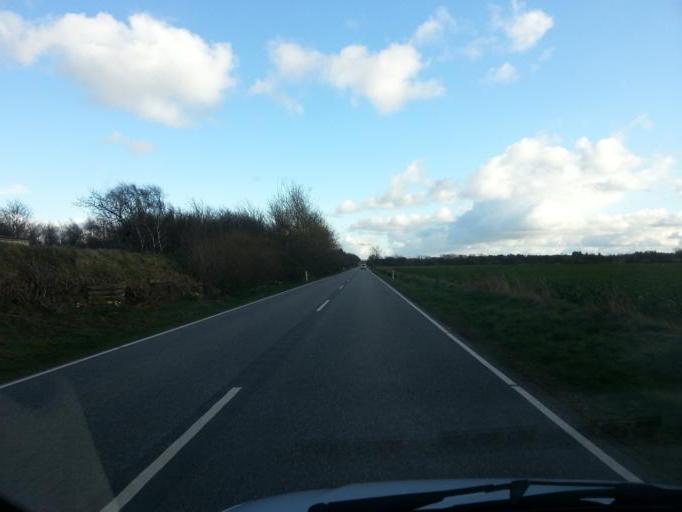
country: DK
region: Central Jutland
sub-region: Ringkobing-Skjern Kommune
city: Tarm
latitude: 55.8803
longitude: 8.5268
